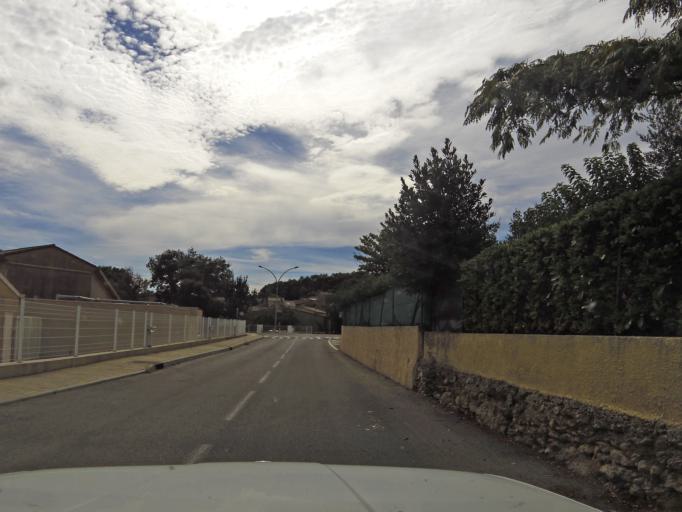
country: FR
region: Languedoc-Roussillon
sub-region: Departement du Gard
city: Bagard
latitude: 44.0740
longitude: 4.0532
